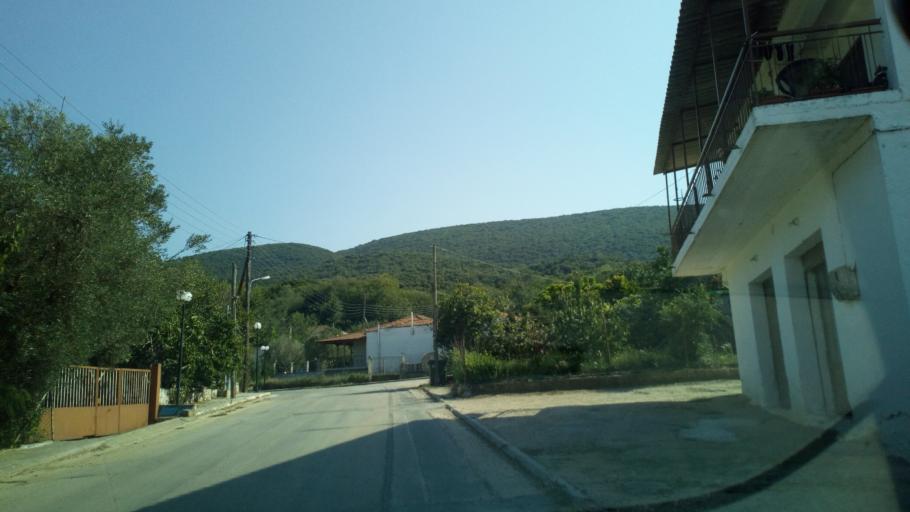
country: GR
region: Central Macedonia
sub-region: Nomos Chalkidikis
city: Galatista
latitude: 40.5059
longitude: 23.3768
